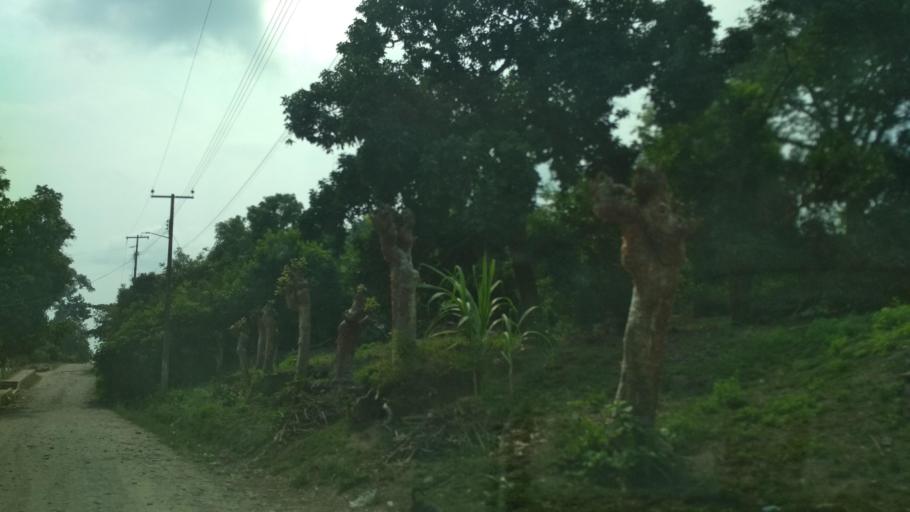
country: MM
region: Kayah
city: Loikaw
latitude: 20.2170
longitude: 97.2849
